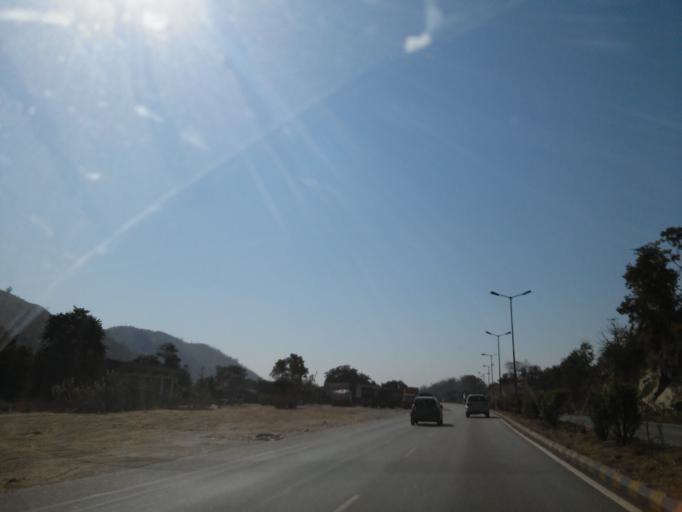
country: IN
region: Rajasthan
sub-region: Udaipur
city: Udaipur
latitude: 24.2658
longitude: 73.6743
